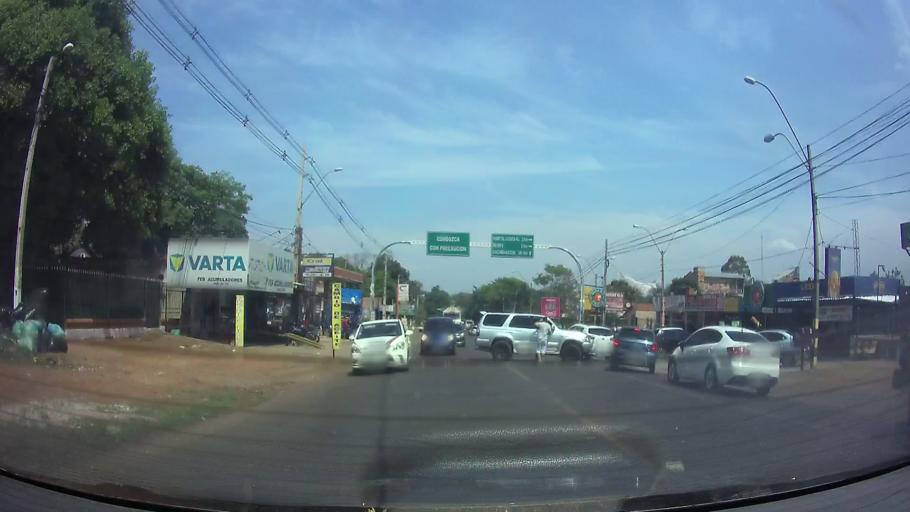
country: PY
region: Central
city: Capiata
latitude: -25.3896
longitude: -57.4700
